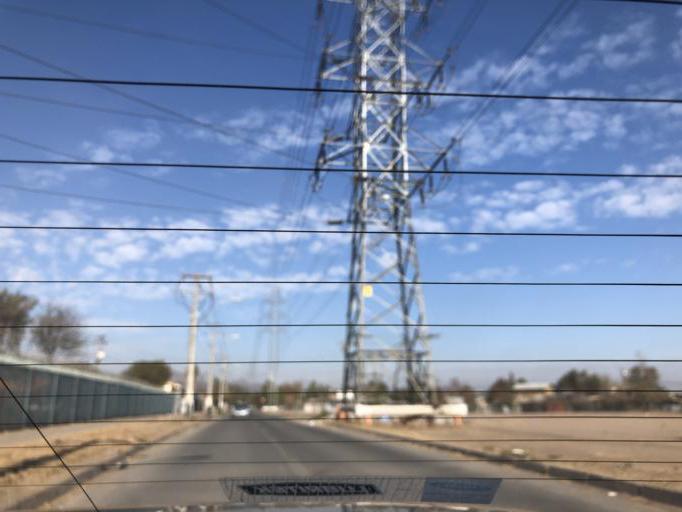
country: CL
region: Santiago Metropolitan
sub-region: Provincia de Santiago
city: La Pintana
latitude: -33.6179
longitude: -70.6171
